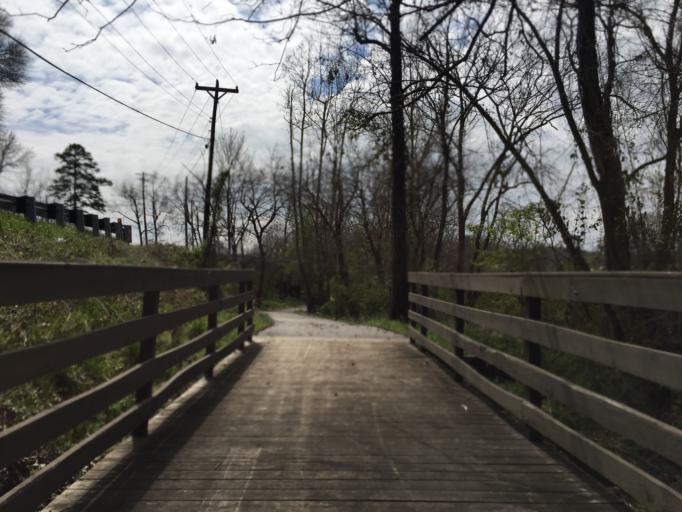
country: US
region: South Carolina
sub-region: Greenville County
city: Mauldin
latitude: 34.7994
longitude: -82.3643
